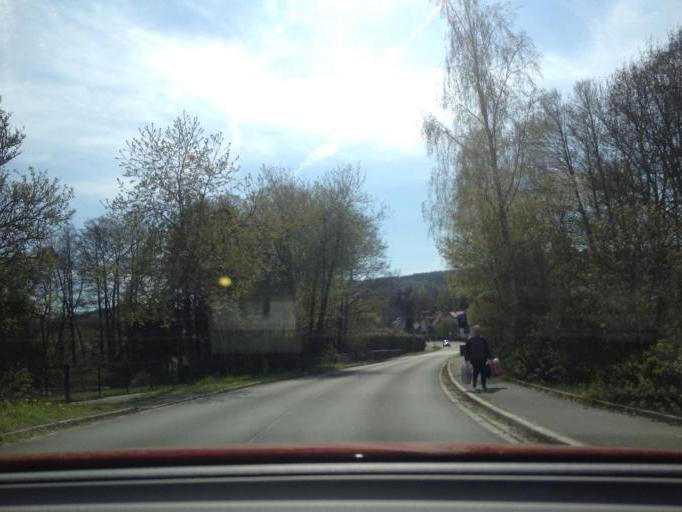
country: DE
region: Bavaria
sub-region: Upper Franconia
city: Gefrees
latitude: 50.0954
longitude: 11.7424
